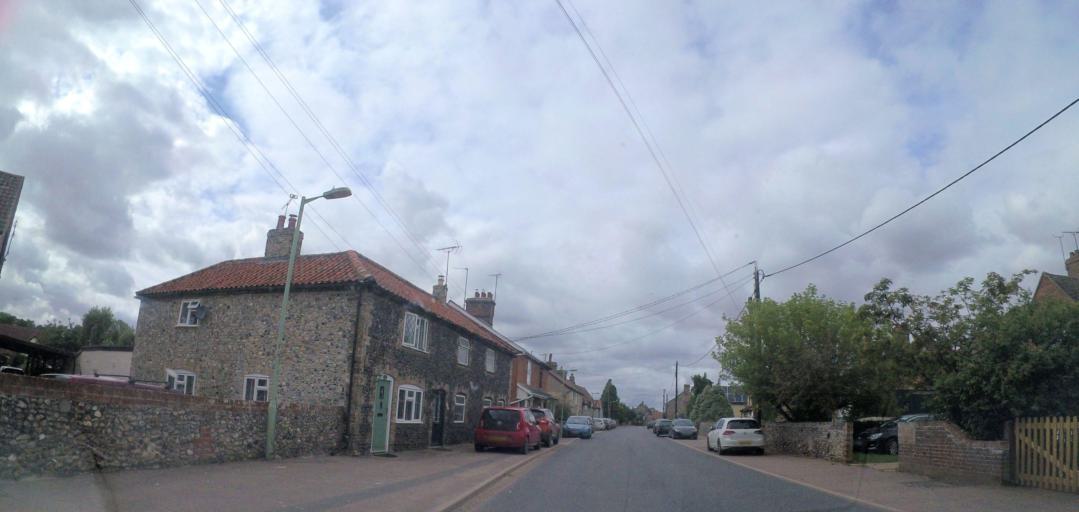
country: GB
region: England
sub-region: Suffolk
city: Lakenheath
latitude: 52.3148
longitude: 0.5453
